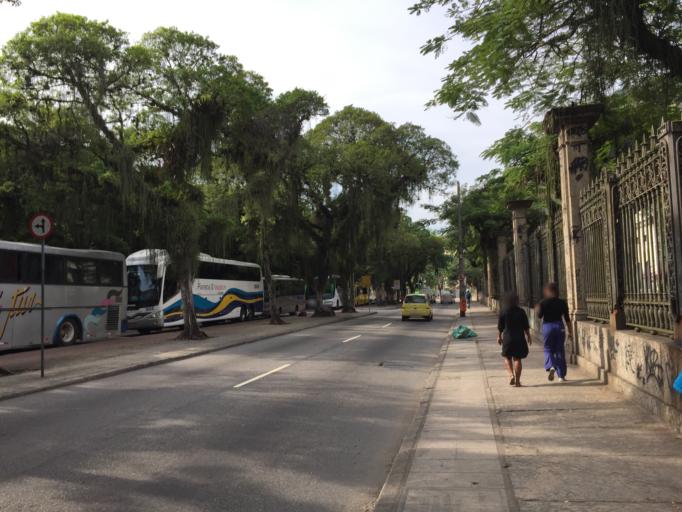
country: BR
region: Rio de Janeiro
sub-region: Rio De Janeiro
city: Rio de Janeiro
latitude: -22.9522
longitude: -43.1739
